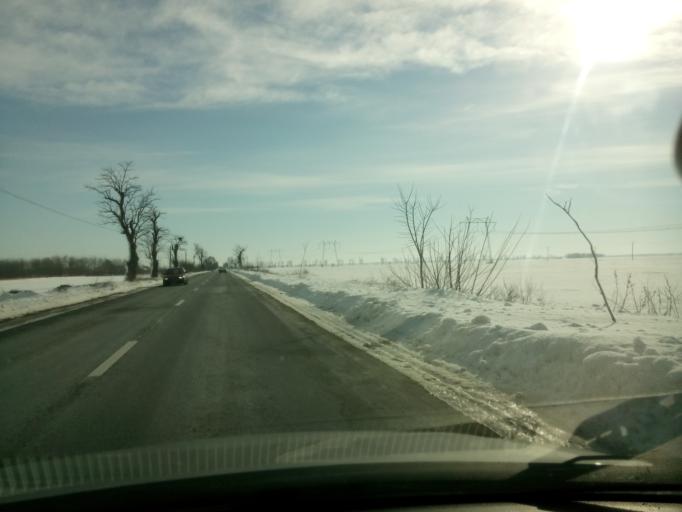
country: RO
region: Calarasi
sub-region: Comuna Frumusani
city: Frumusani
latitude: 44.2607
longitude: 26.3569
